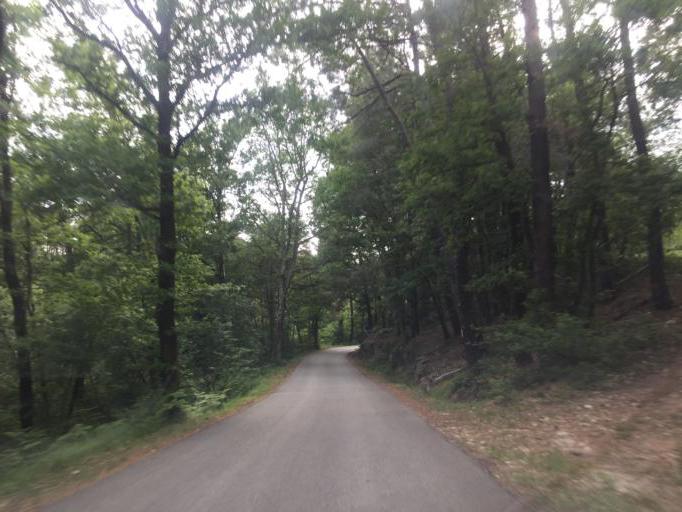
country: FR
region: Rhone-Alpes
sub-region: Departement de l'Ardeche
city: Privas
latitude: 44.7533
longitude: 4.5962
